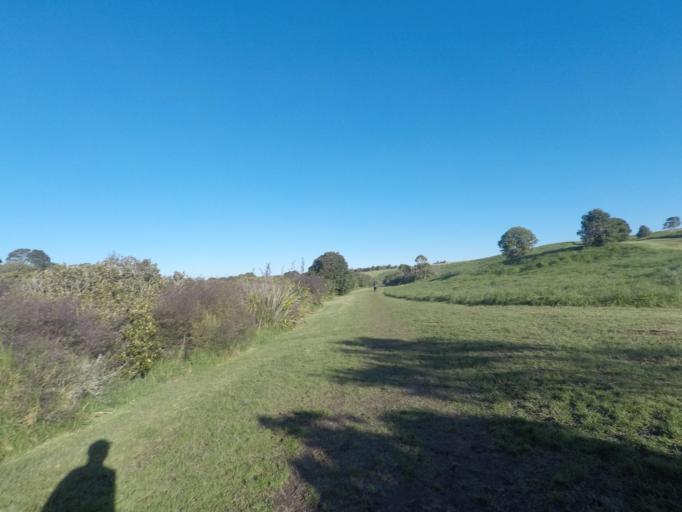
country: NZ
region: Auckland
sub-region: Auckland
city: Rosebank
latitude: -36.8549
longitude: 174.7111
